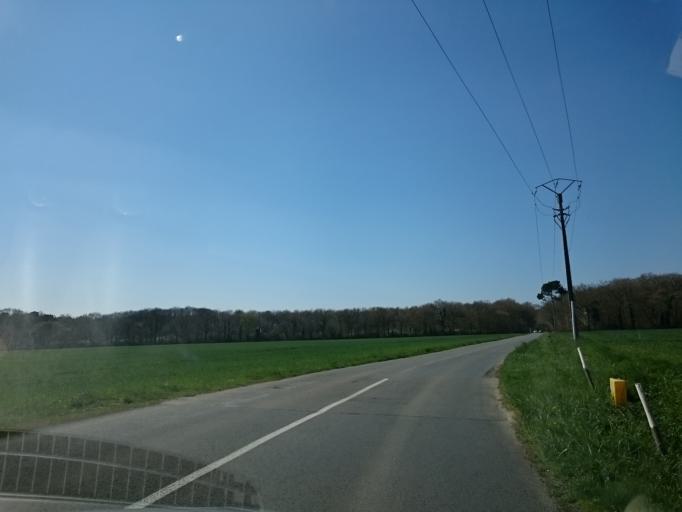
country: FR
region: Brittany
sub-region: Departement d'Ille-et-Vilaine
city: Orgeres
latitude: 48.0022
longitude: -1.6783
